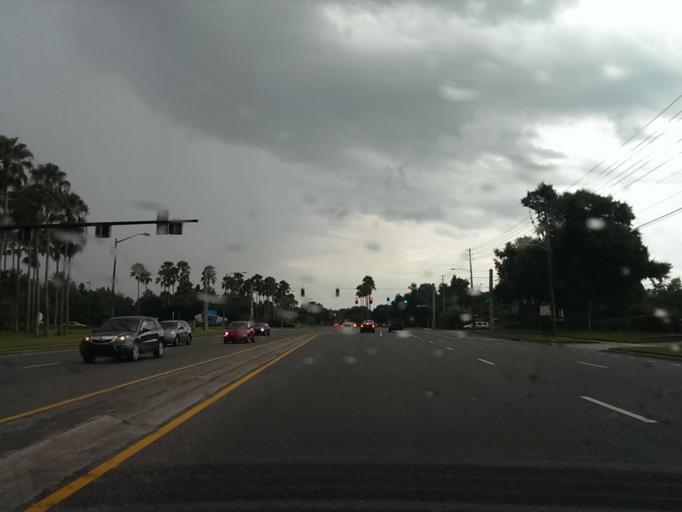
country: US
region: Florida
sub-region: Orange County
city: Tangelo Park
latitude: 28.4829
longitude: -81.4627
